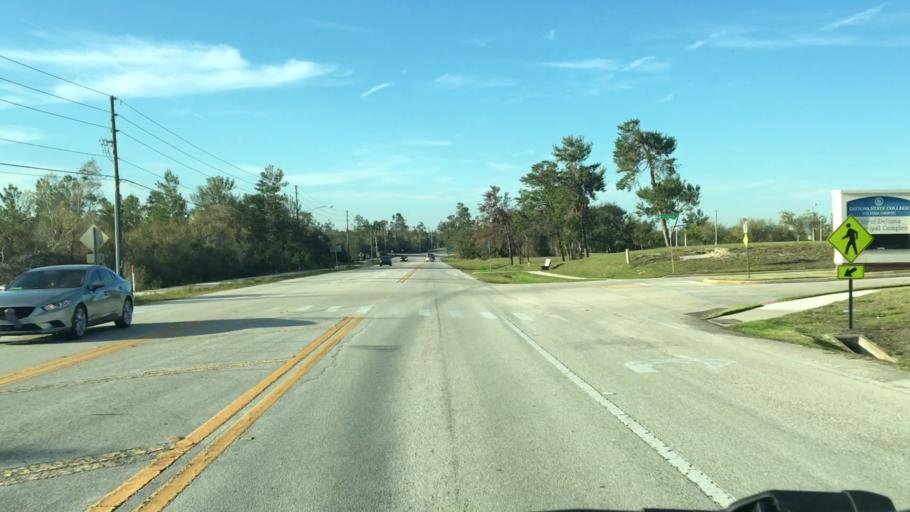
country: US
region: Florida
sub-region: Volusia County
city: Deltona
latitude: 28.9278
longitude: -81.2227
